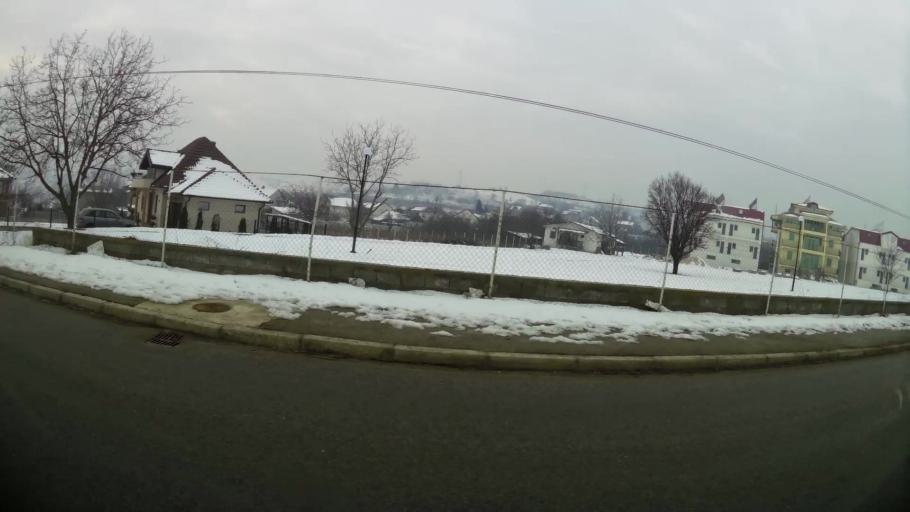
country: MK
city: Kondovo
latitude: 42.0343
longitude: 21.3433
